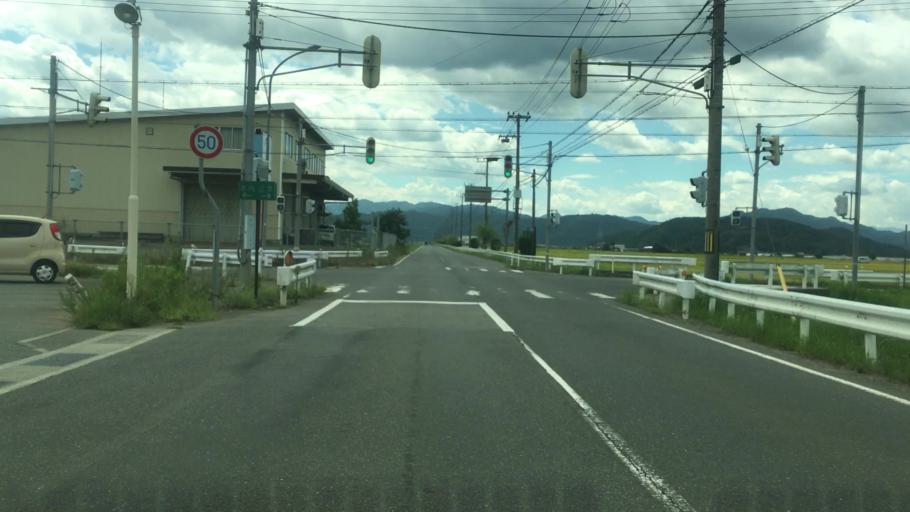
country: JP
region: Hyogo
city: Toyooka
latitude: 35.5250
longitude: 134.8398
